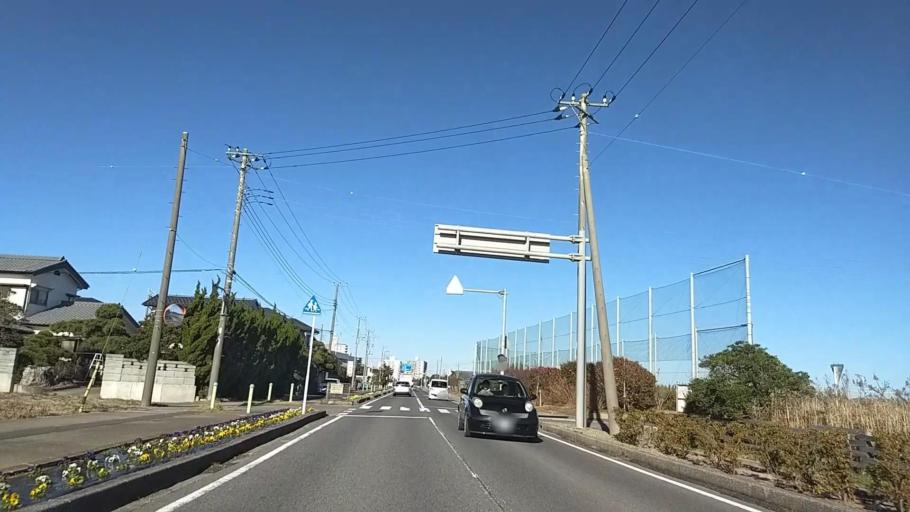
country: JP
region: Chiba
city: Mobara
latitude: 35.4423
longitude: 140.3999
